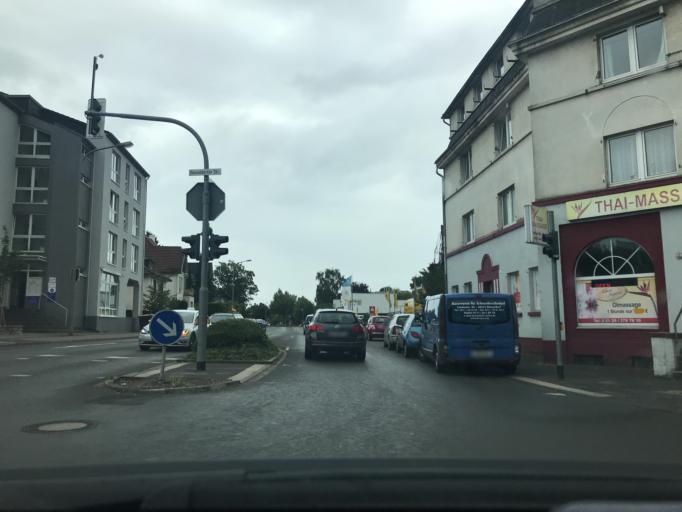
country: DE
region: North Rhine-Westphalia
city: Haan
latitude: 51.1867
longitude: 6.9902
